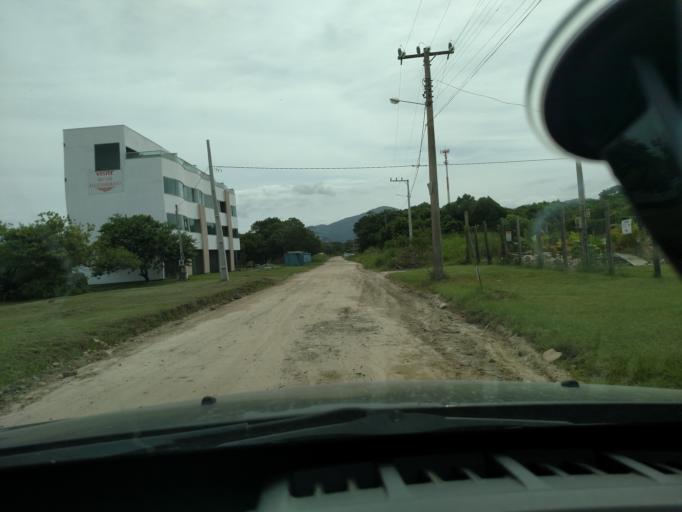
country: BR
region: Santa Catarina
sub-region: Porto Belo
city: Porto Belo
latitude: -27.1836
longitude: -48.5038
